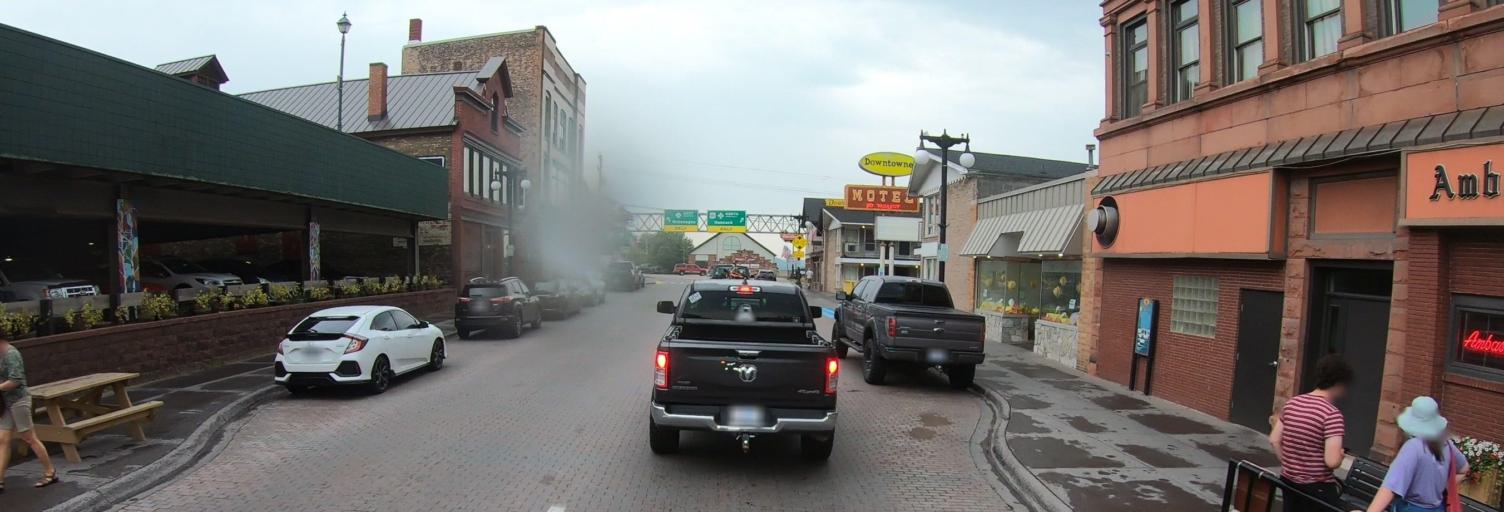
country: US
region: Michigan
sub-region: Houghton County
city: Houghton
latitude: 47.1219
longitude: -88.5720
